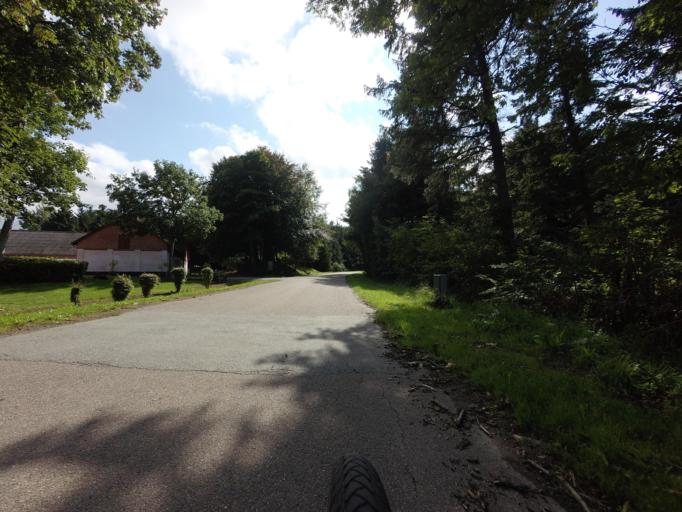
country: DK
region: North Denmark
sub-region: Hjorring Kommune
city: Hjorring
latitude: 57.5395
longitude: 10.0588
